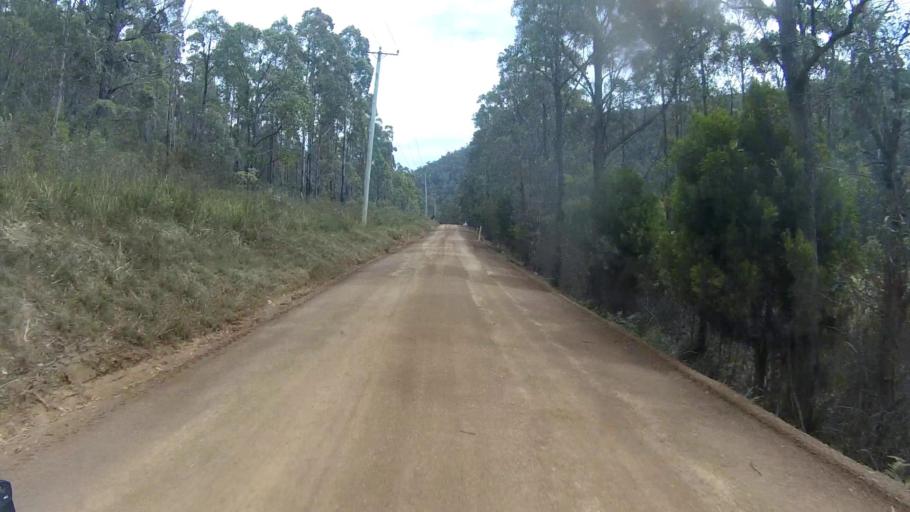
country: AU
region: Tasmania
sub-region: Sorell
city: Sorell
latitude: -42.7455
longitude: 147.7809
